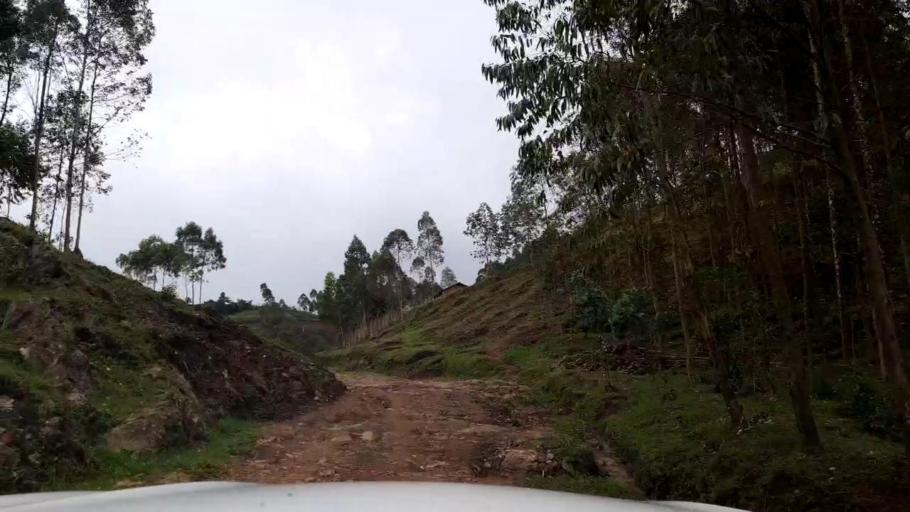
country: RW
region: Northern Province
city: Musanze
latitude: -1.6092
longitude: 29.7674
